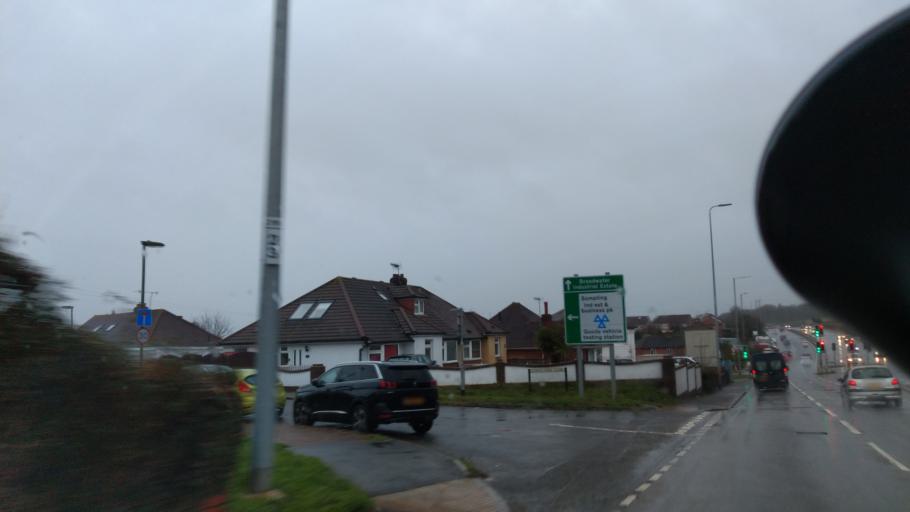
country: GB
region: England
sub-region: West Sussex
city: Lancing
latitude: 50.8373
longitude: -0.3347
